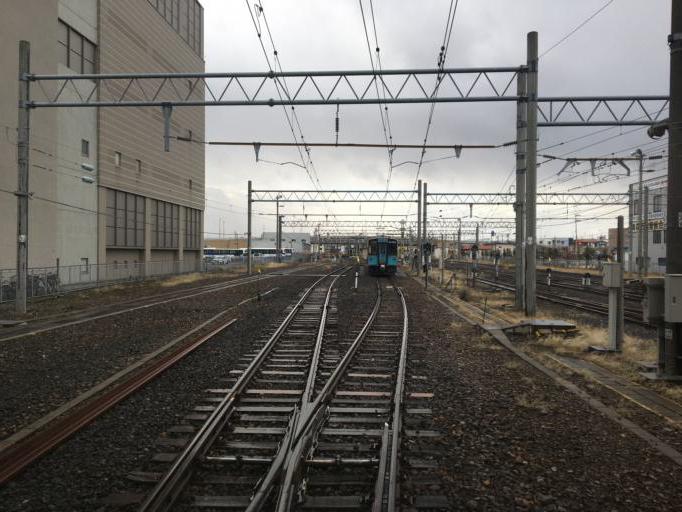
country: JP
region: Aomori
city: Aomori Shi
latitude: 40.8270
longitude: 140.7330
